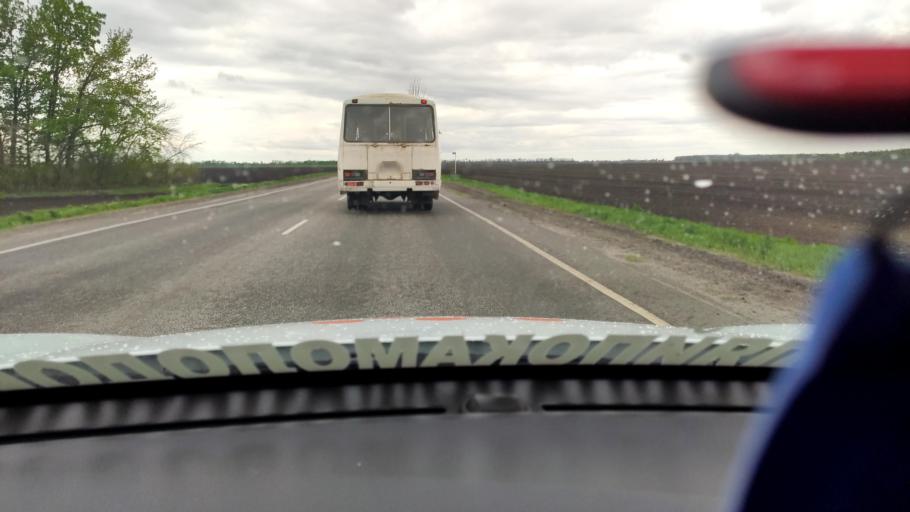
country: RU
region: Voronezj
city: Liski
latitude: 51.0344
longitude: 39.6225
